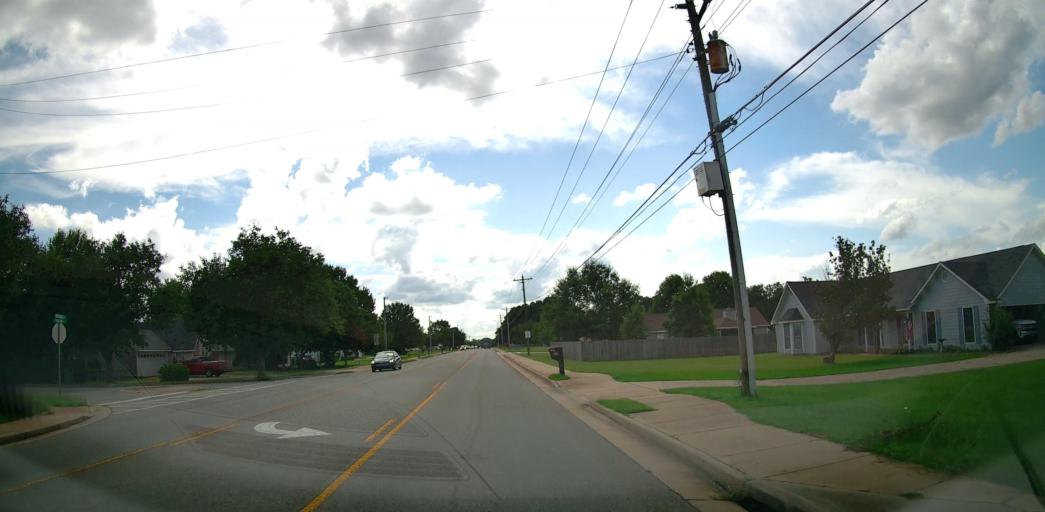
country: US
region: Georgia
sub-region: Houston County
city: Centerville
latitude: 32.5710
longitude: -83.6786
